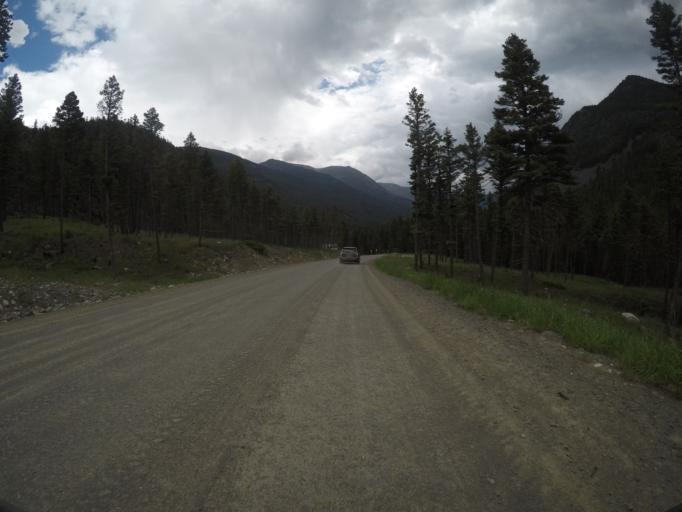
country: US
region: Montana
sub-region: Park County
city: Livingston
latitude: 45.4769
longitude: -110.2063
